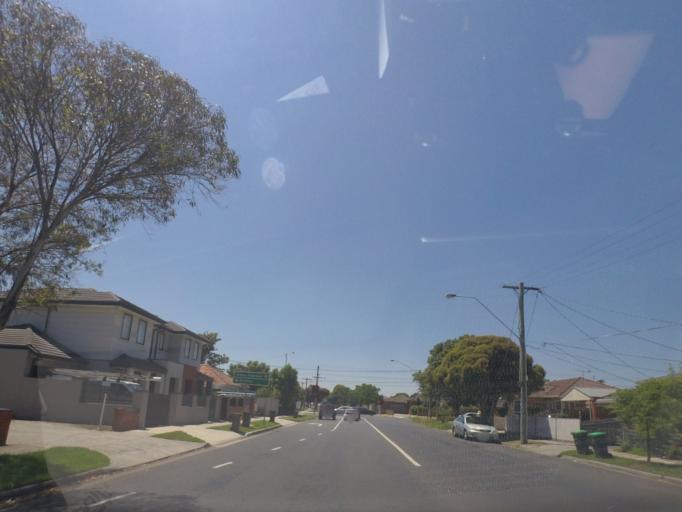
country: AU
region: Victoria
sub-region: Moreland
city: Hadfield
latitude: -37.7175
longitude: 144.9407
